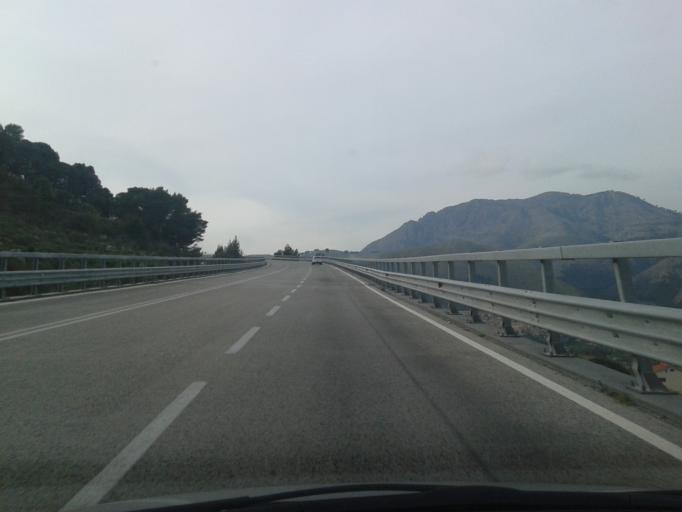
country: IT
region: Sicily
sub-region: Palermo
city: Giacalone
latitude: 38.0370
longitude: 13.2412
